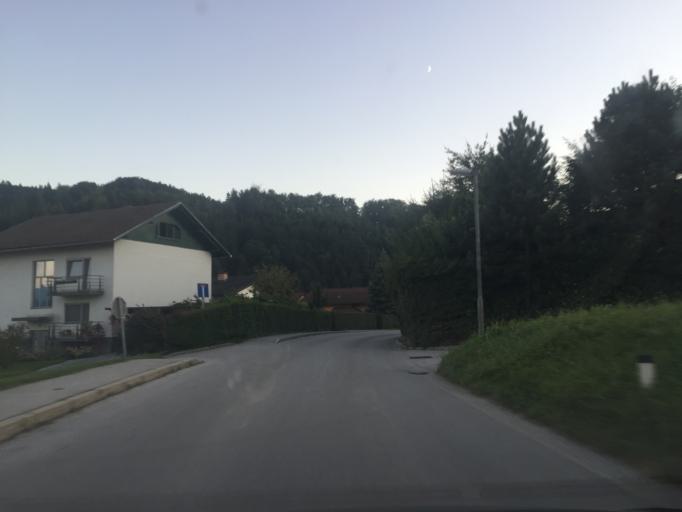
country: SI
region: Sostanj
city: Sostanj
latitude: 46.3840
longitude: 15.0312
